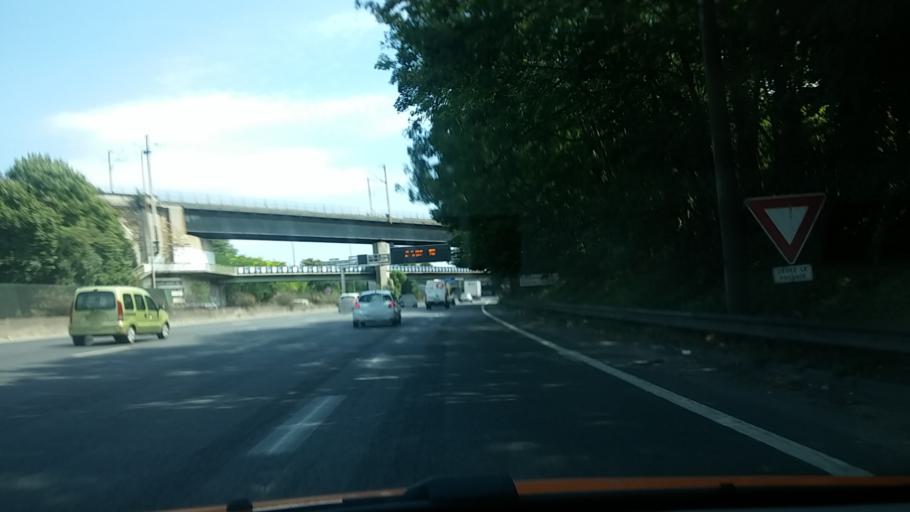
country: FR
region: Ile-de-France
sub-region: Departement du Val-de-Marne
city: Champigny-sur-Marne
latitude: 48.8298
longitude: 2.4967
